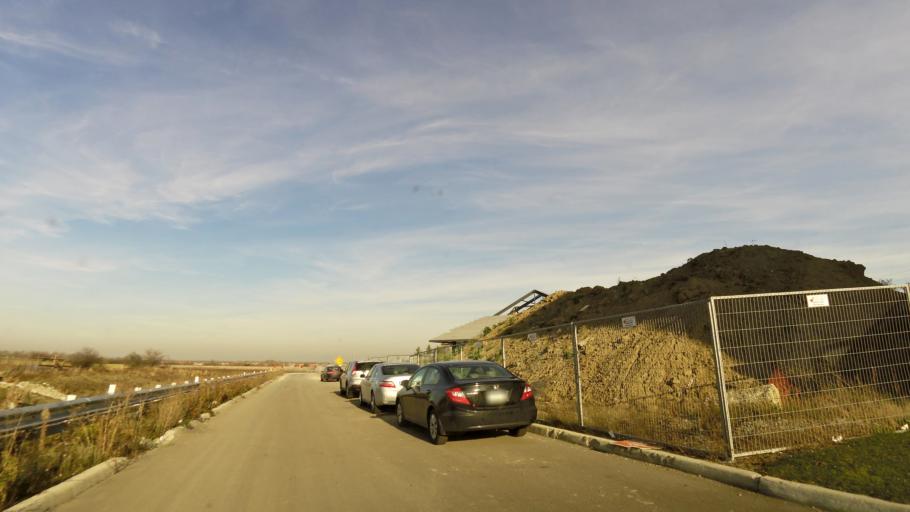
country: CA
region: Ontario
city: Brampton
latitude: 43.7761
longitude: -79.7606
